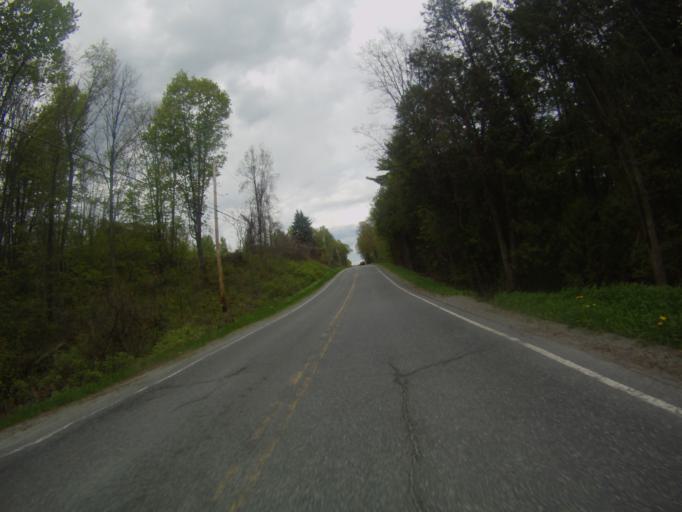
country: US
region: New York
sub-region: Essex County
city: Port Henry
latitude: 44.0294
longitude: -73.5017
